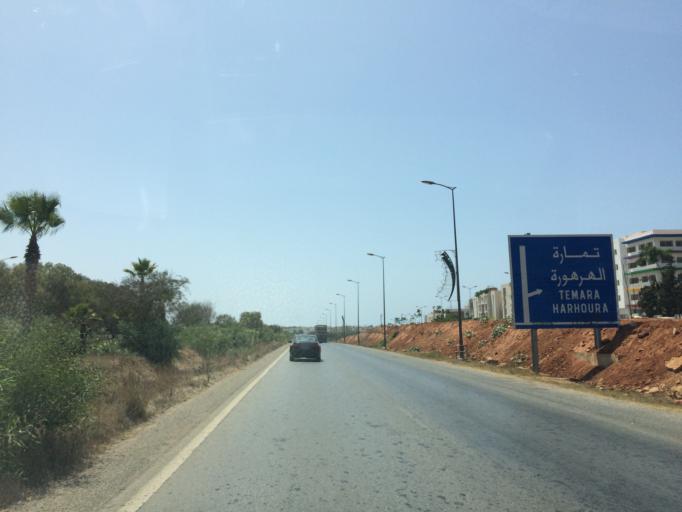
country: MA
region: Rabat-Sale-Zemmour-Zaer
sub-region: Skhirate-Temara
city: Temara
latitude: 33.9658
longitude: -6.8930
